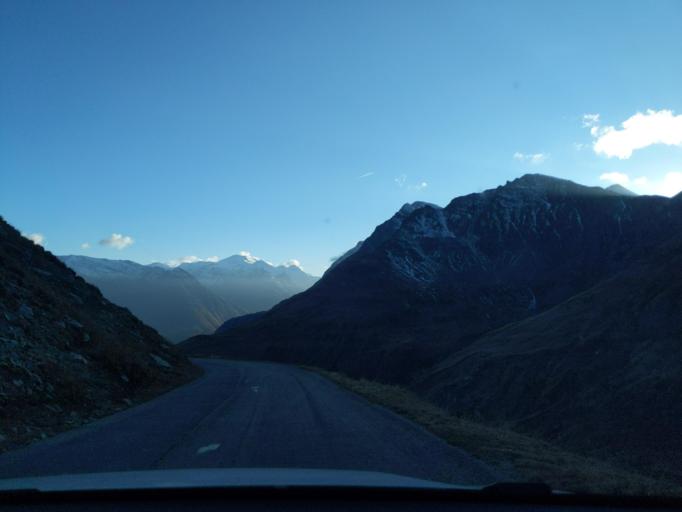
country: FR
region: Rhone-Alpes
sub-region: Departement de la Savoie
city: Val-d'Isere
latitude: 45.3985
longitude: 7.0427
